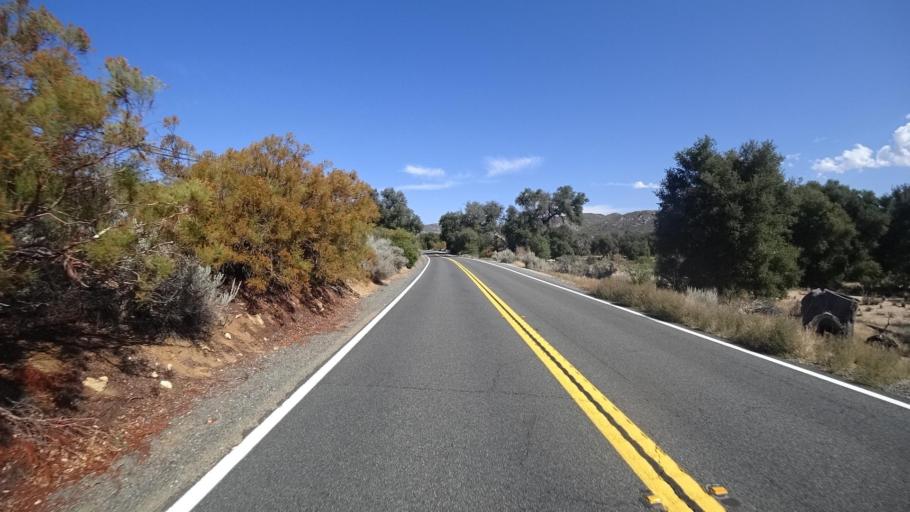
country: US
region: California
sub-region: Riverside County
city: Aguanga
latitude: 33.3268
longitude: -116.7024
